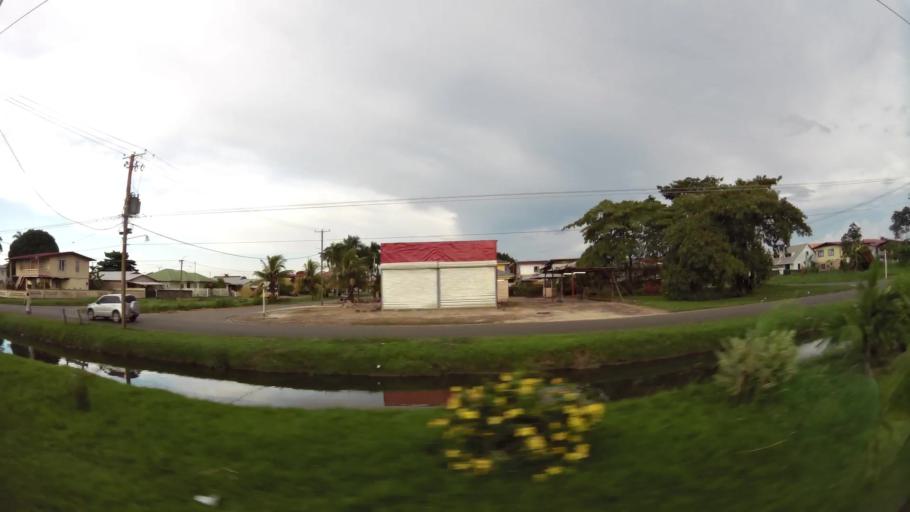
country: SR
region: Paramaribo
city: Paramaribo
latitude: 5.8423
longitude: -55.1386
